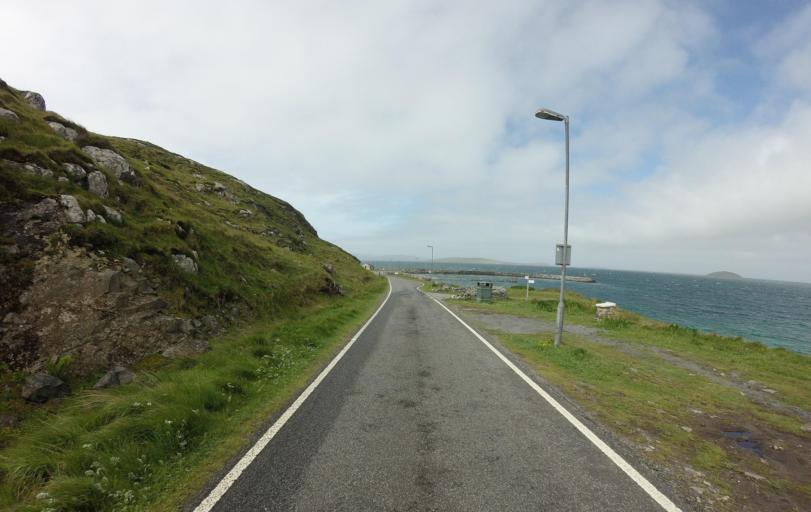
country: GB
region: Scotland
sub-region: Eilean Siar
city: Isle of South Uist
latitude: 57.0719
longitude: -7.3050
